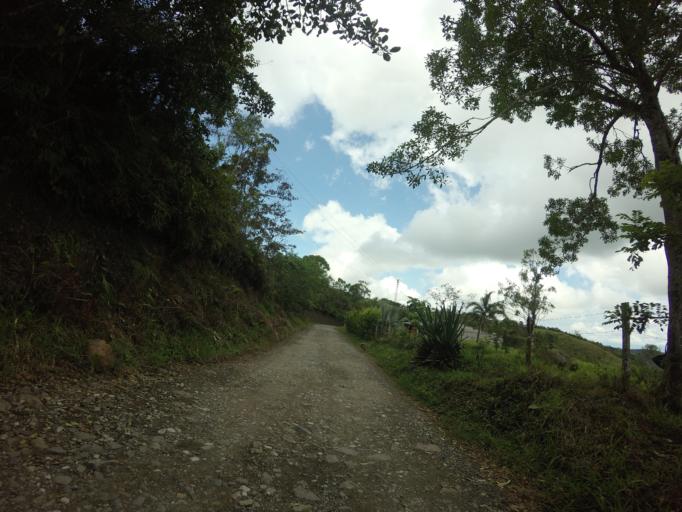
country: CO
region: Caldas
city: Victoria
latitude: 5.3152
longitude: -74.9536
